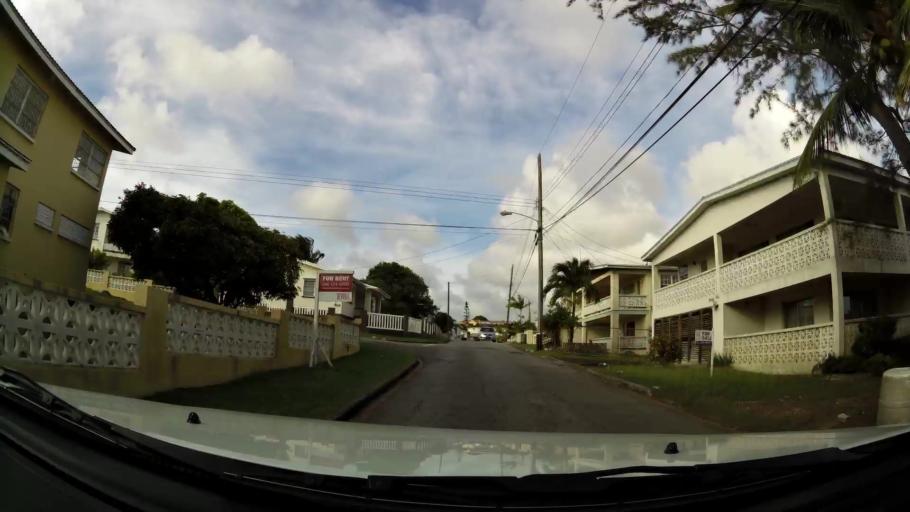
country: BB
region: Christ Church
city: Oistins
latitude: 13.0893
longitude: -59.5705
